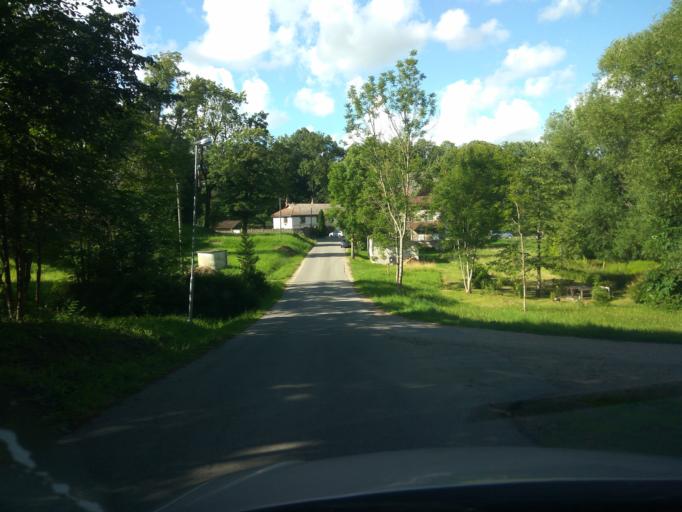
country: LV
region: Aizpute
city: Aizpute
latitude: 56.7202
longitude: 21.5962
